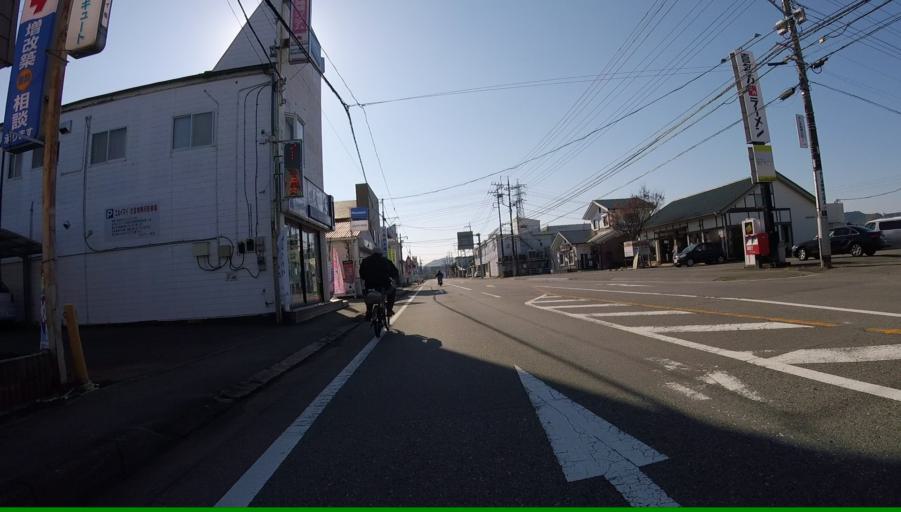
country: JP
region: Shizuoka
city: Mishima
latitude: 35.1078
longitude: 138.9157
